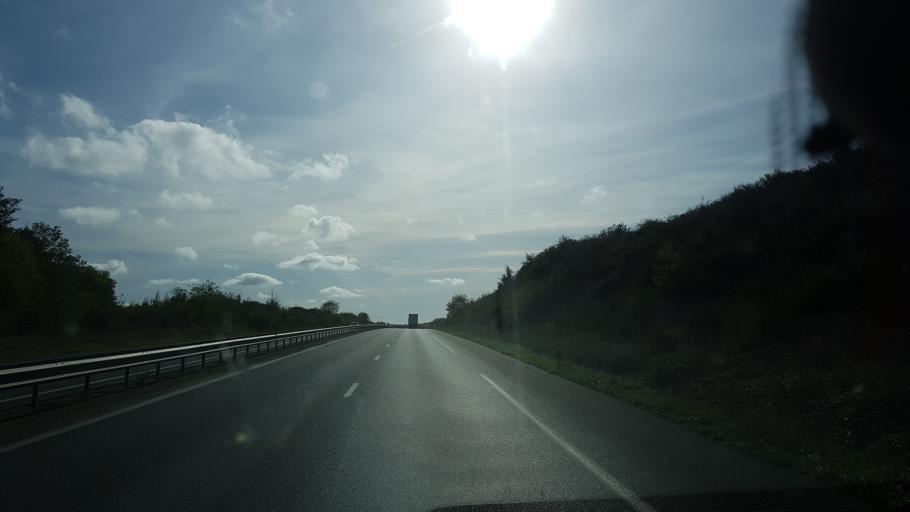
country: FR
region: Poitou-Charentes
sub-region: Departement de la Charente
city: Taponnat-Fleurignac
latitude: 45.7689
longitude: 0.3994
